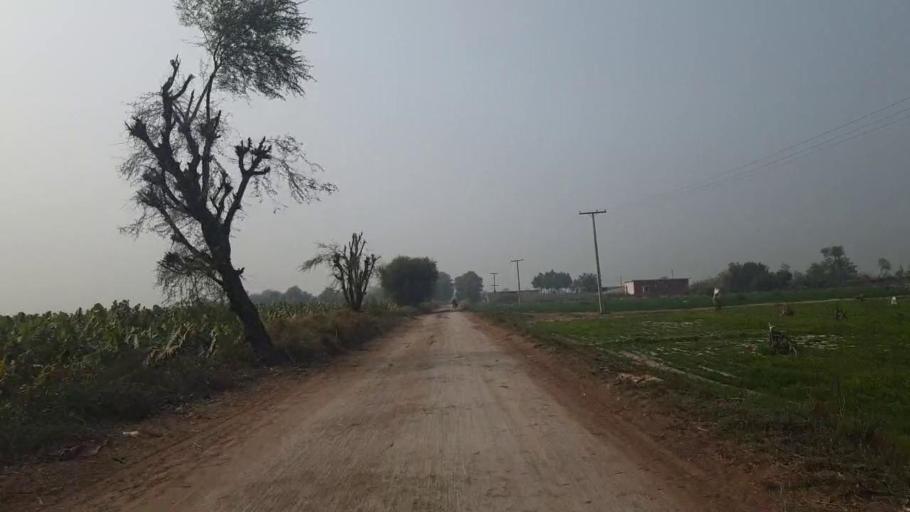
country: PK
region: Sindh
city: Bhit Shah
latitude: 25.7738
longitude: 68.5658
